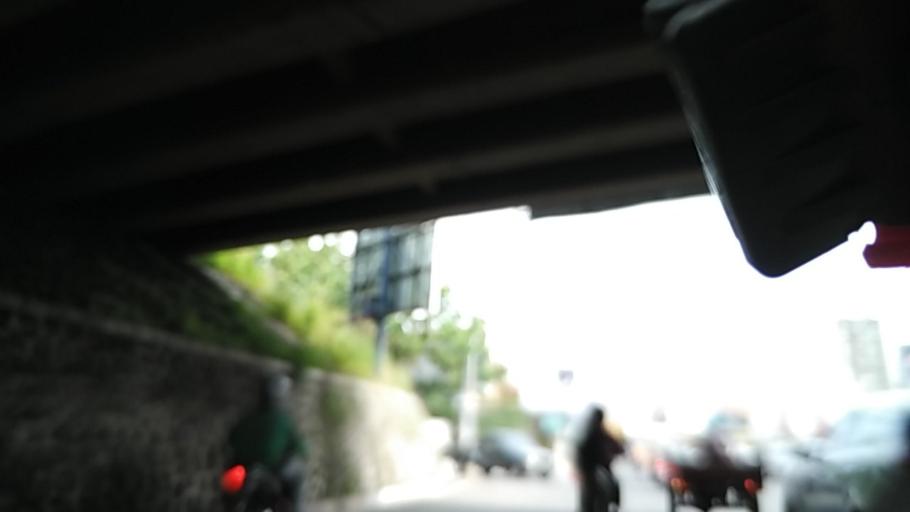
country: ID
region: Central Java
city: Semarang
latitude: -7.0533
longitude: 110.4300
